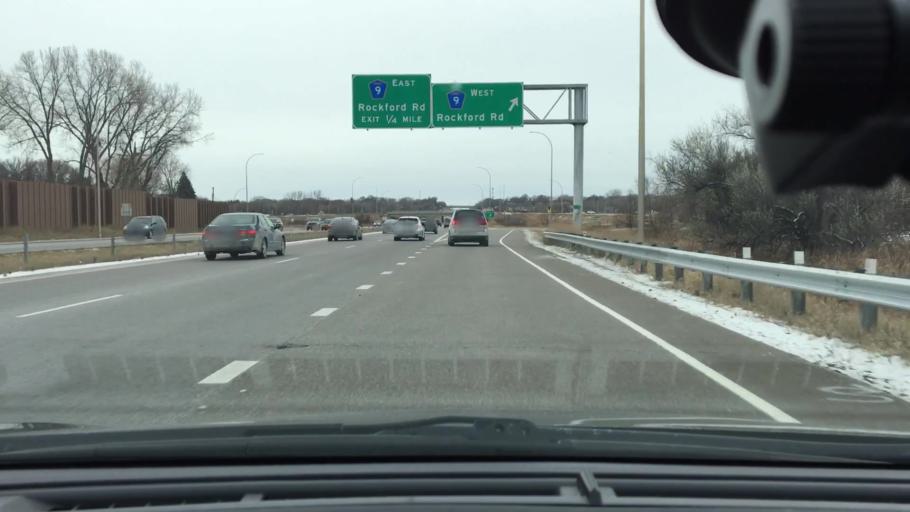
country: US
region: Minnesota
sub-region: Hennepin County
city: New Hope
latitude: 45.0377
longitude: -93.4010
